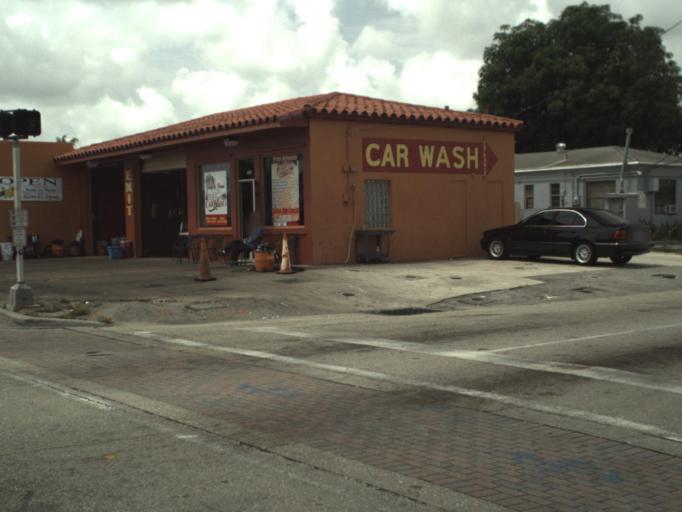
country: US
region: Florida
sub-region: Broward County
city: Hallandale Beach
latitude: 25.9894
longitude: -80.1425
